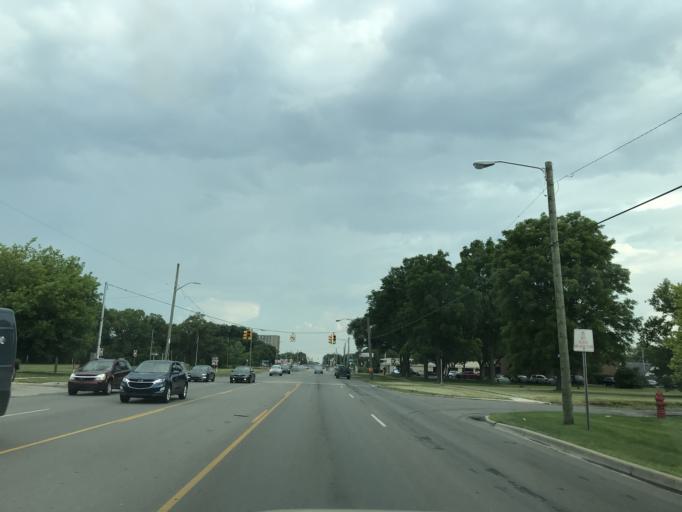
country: US
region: Michigan
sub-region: Wayne County
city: Allen Park
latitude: 42.2313
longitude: -83.2301
